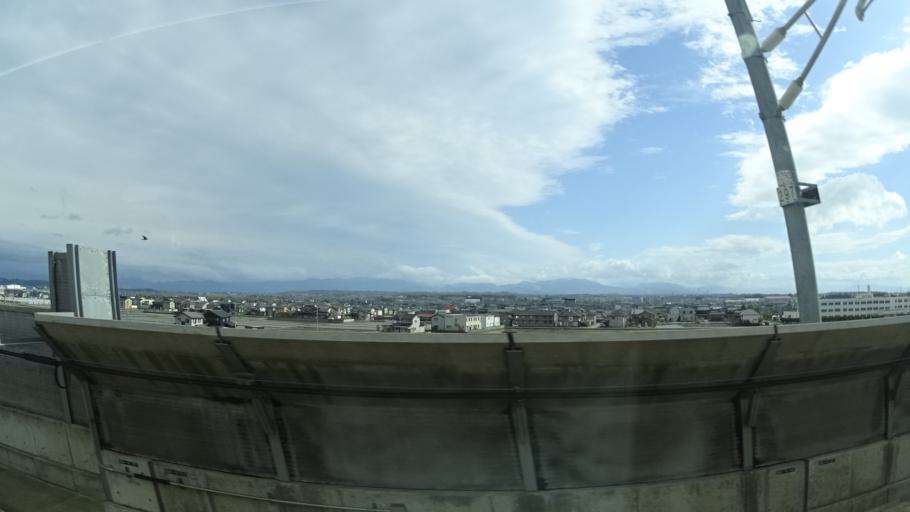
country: JP
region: Toyama
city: Kuragaki-kosugi
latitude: 36.7277
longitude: 137.1072
